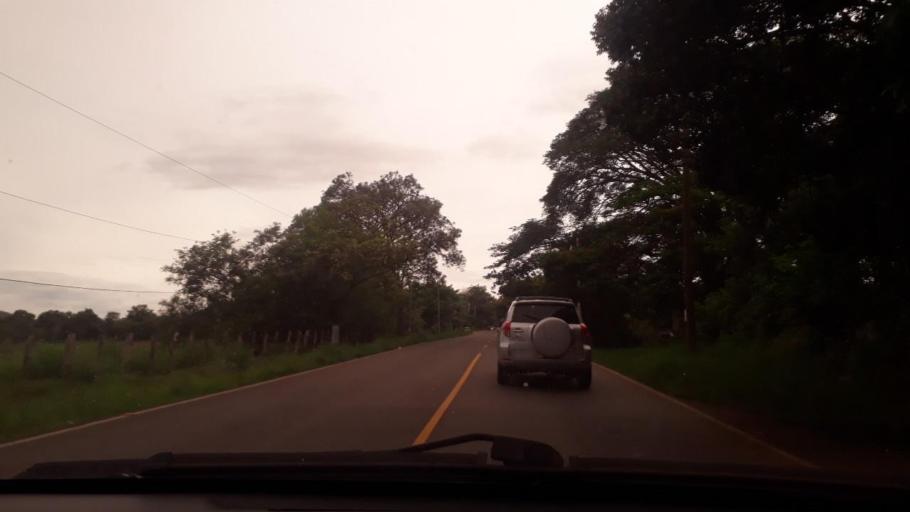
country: GT
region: Jutiapa
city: Asuncion Mita
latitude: 14.3545
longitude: -89.7604
